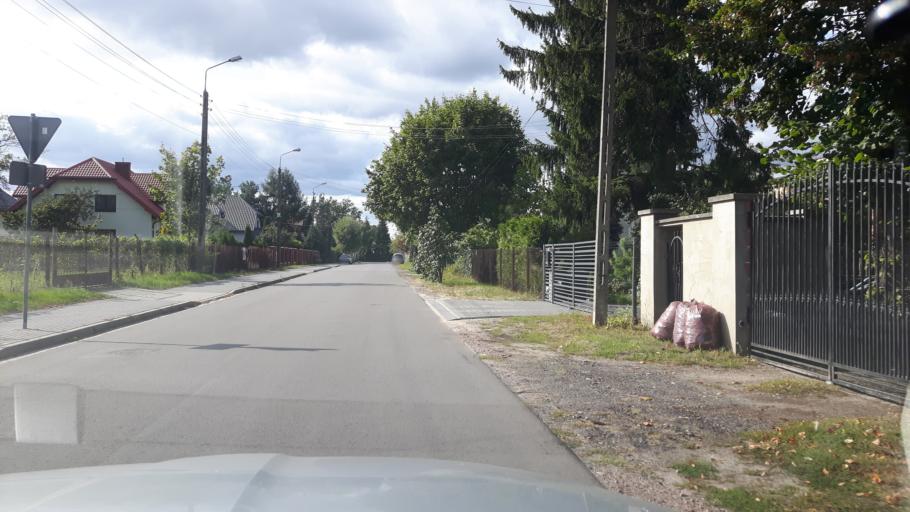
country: PL
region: Masovian Voivodeship
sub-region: Powiat wolominski
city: Kobylka
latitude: 52.3358
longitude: 21.2031
